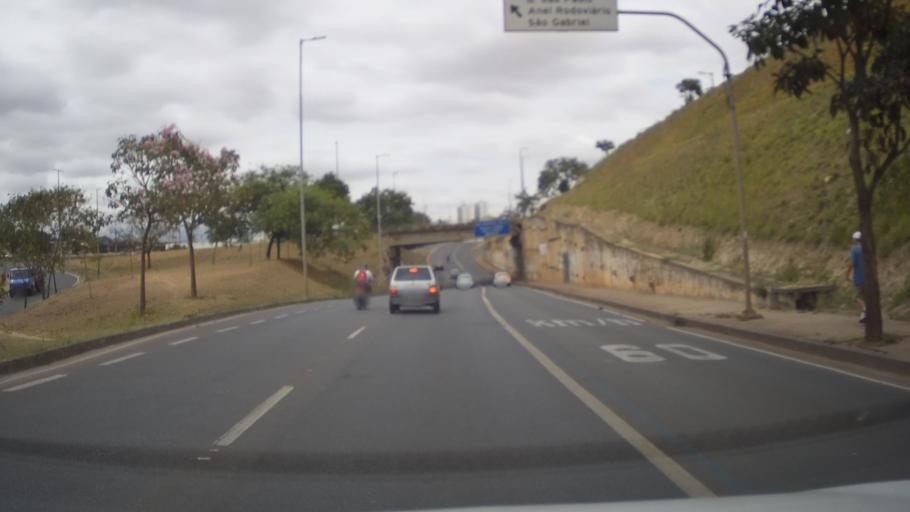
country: BR
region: Minas Gerais
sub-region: Belo Horizonte
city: Belo Horizonte
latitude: -19.8593
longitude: -43.9248
